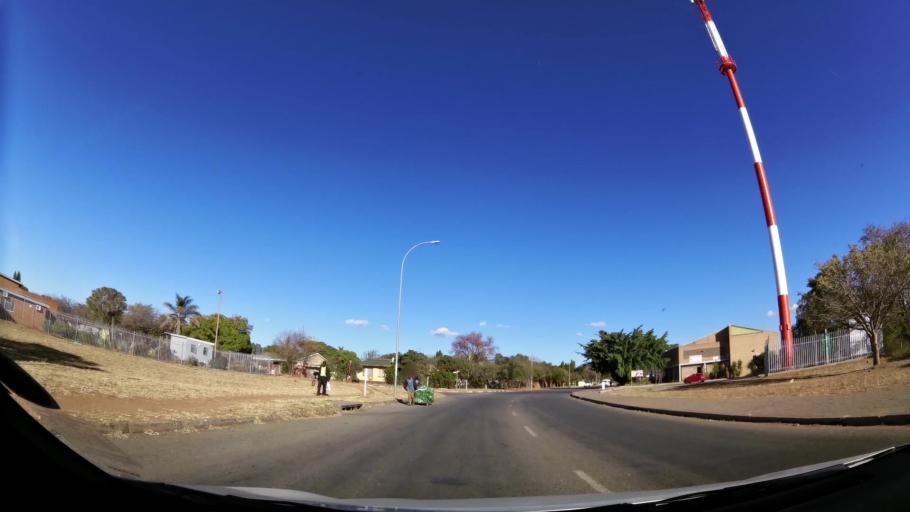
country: ZA
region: Limpopo
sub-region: Capricorn District Municipality
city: Polokwane
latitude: -23.8918
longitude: 29.4627
